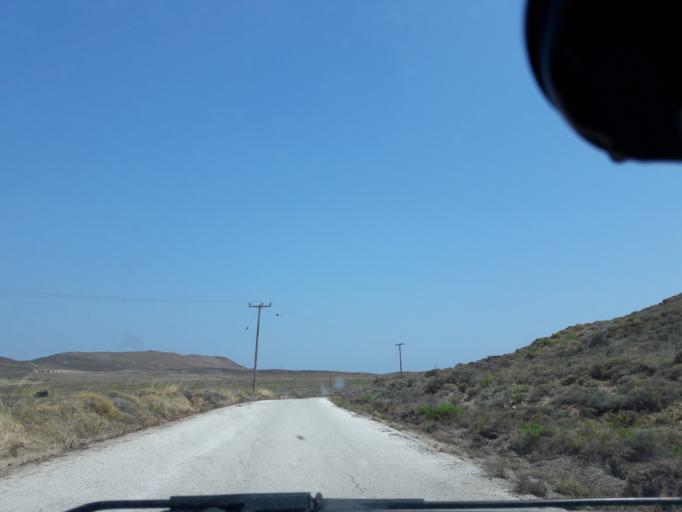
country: GR
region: North Aegean
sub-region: Nomos Lesvou
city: Myrina
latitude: 39.9749
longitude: 25.3533
